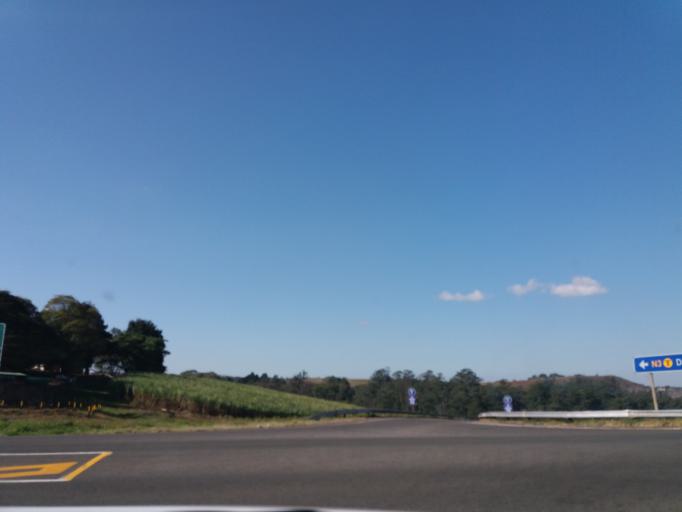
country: ZA
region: KwaZulu-Natal
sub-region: eThekwini Metropolitan Municipality
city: Mpumalanga
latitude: -29.8031
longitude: 30.7458
